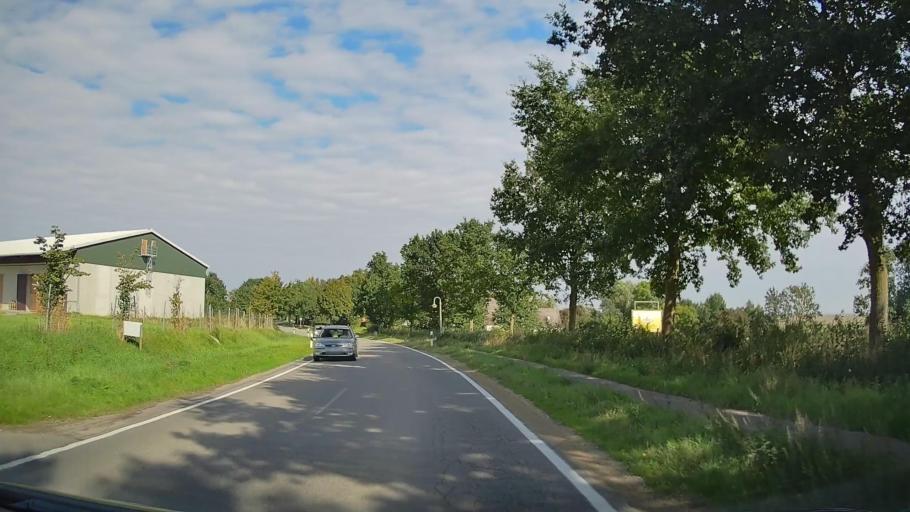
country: DE
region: Schleswig-Holstein
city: Oldenburg in Holstein
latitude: 54.3285
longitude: 10.8921
